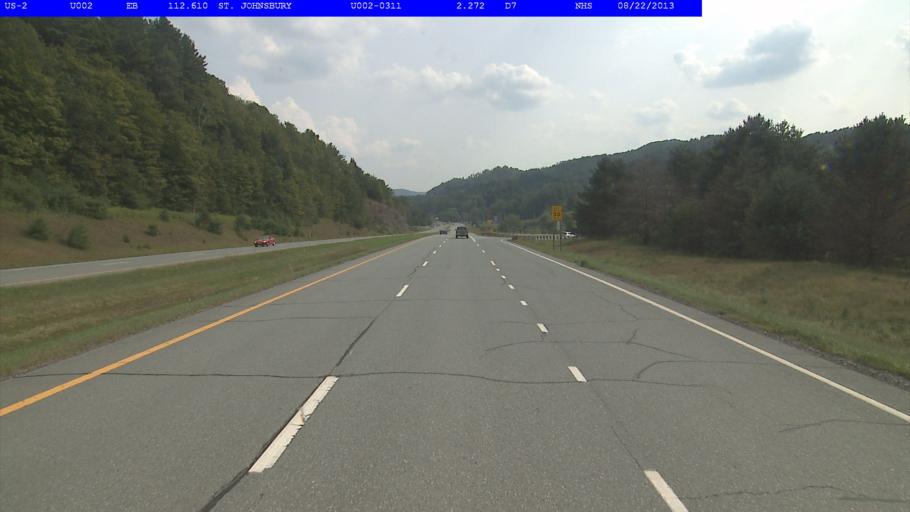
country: US
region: Vermont
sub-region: Caledonia County
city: St Johnsbury
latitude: 44.4252
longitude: -72.0308
